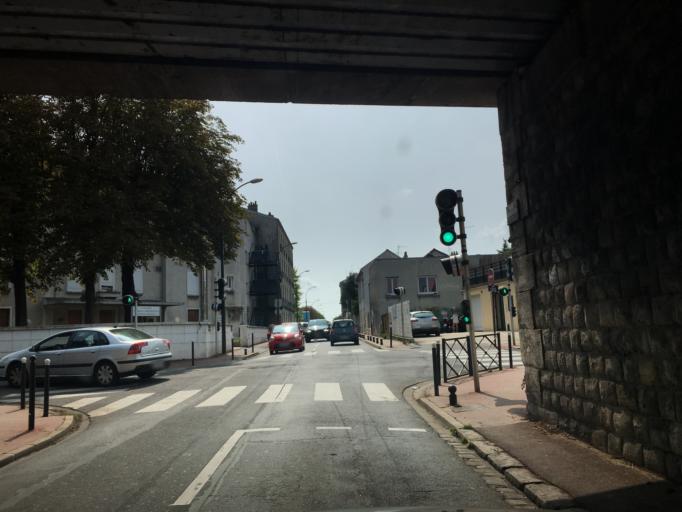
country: FR
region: Ile-de-France
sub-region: Departement du Val-de-Marne
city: Saint-Maur-des-Fosses
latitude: 48.8052
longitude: 2.4779
